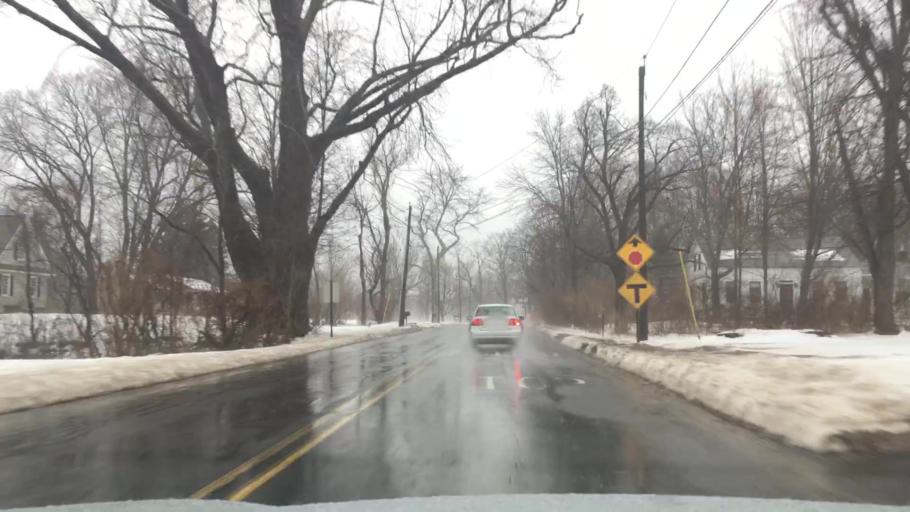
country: US
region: Massachusetts
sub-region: Hampshire County
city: Granby
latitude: 42.2244
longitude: -72.4971
